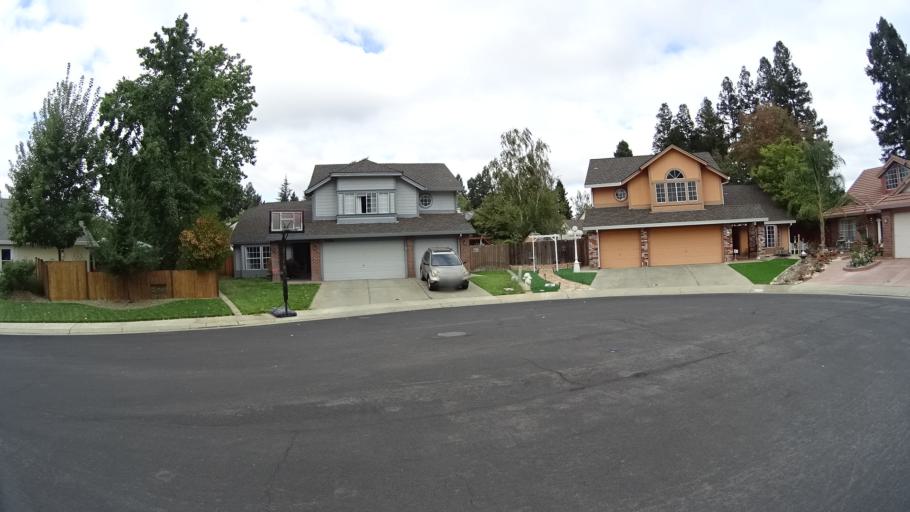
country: US
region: California
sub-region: Sacramento County
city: Laguna
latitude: 38.4158
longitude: -121.4290
